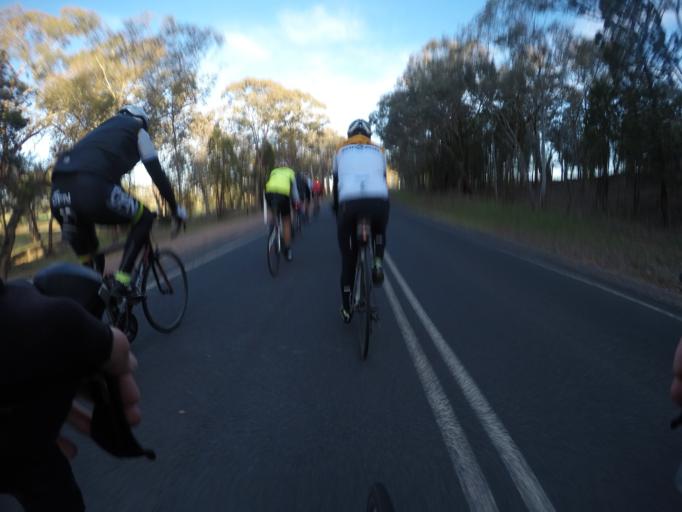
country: AU
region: New South Wales
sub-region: Cabonne
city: Molong
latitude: -33.0560
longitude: 148.8204
